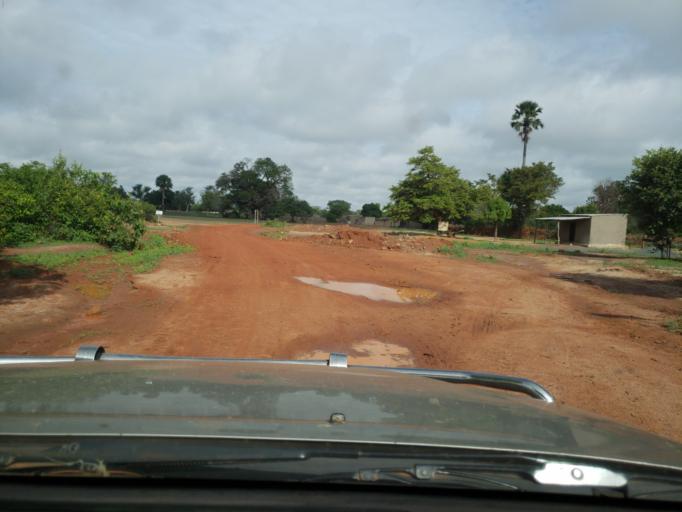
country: ML
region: Sikasso
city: Koutiala
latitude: 12.3925
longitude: -6.0213
